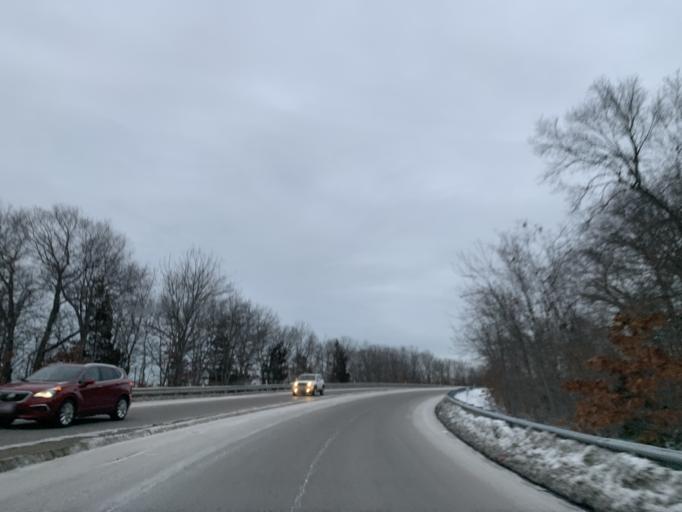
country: US
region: Massachusetts
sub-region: Norfolk County
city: Avon
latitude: 42.0951
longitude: -71.0574
